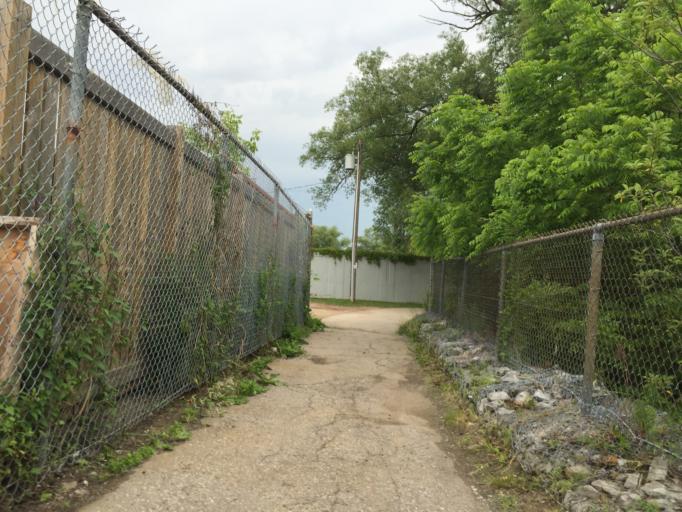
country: CA
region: Ontario
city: Oshawa
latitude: 43.8983
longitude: -78.8697
